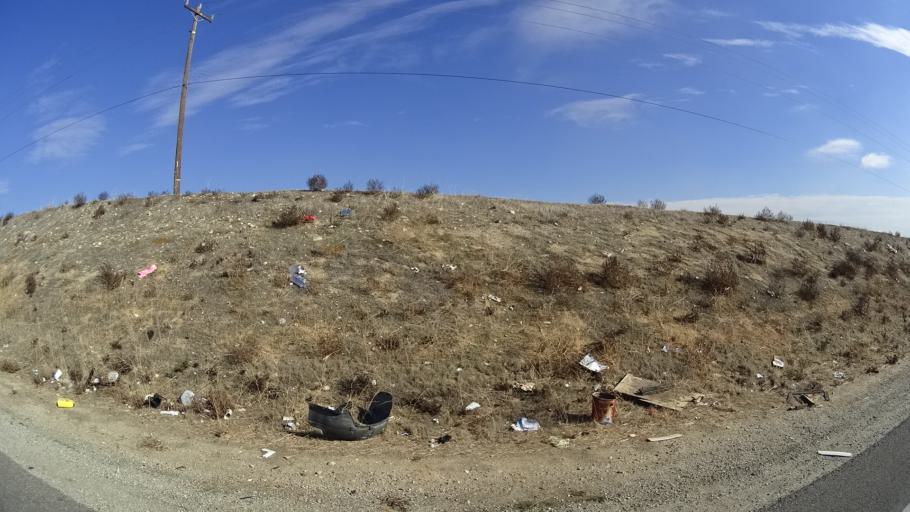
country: US
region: California
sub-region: Kern County
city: Bakersfield
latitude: 35.3871
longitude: -118.9143
